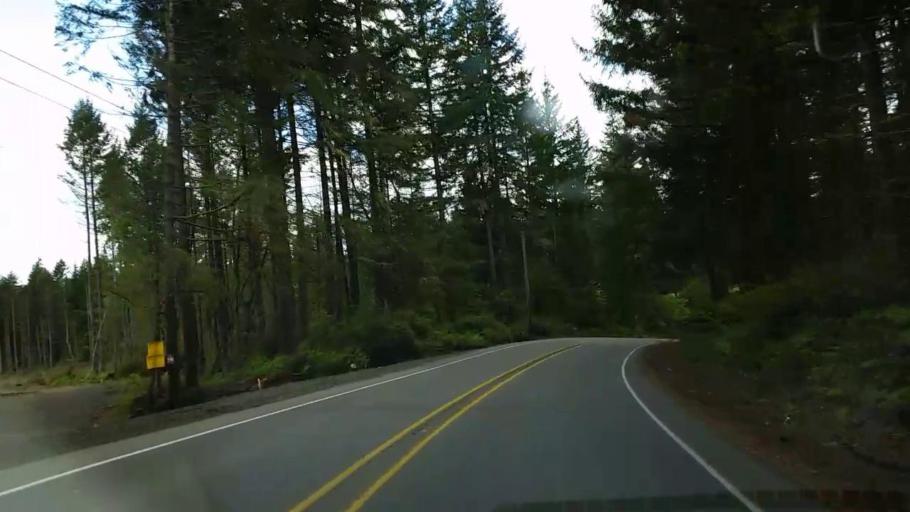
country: US
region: Washington
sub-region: Pierce County
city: Key Center
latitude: 47.3675
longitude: -122.7716
